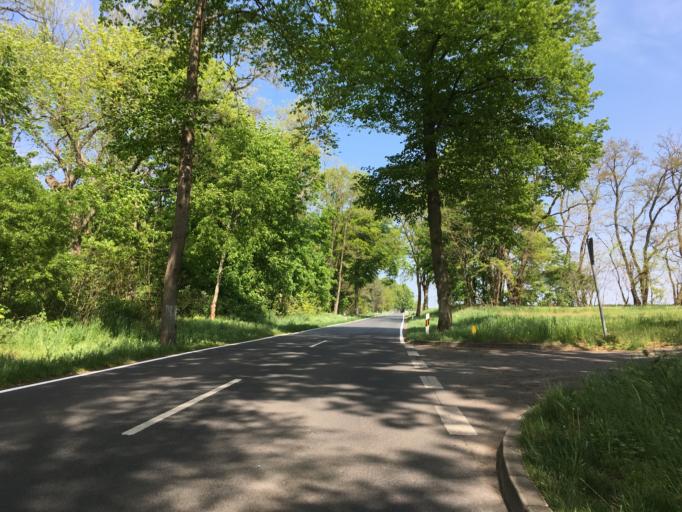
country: DE
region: Brandenburg
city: Melchow
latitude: 52.7129
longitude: 13.7139
